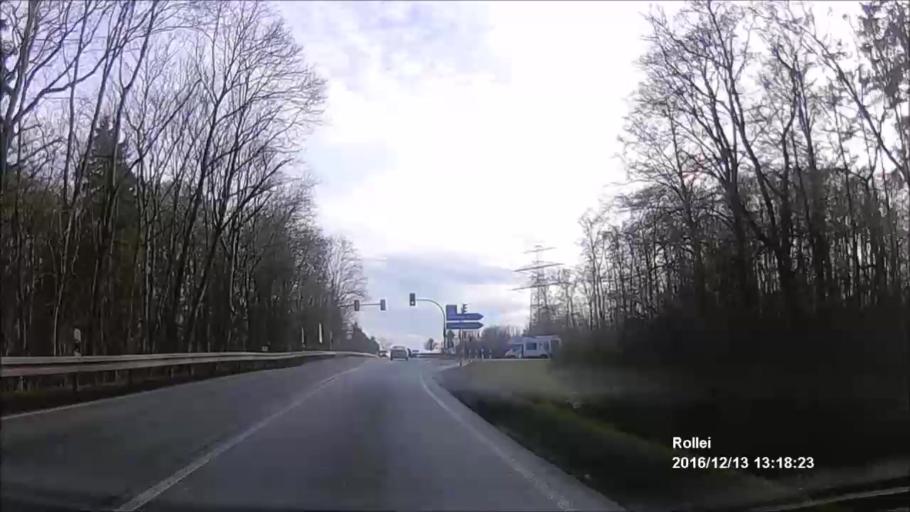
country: DE
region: Thuringia
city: Klettbach
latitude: 50.9284
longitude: 11.1370
